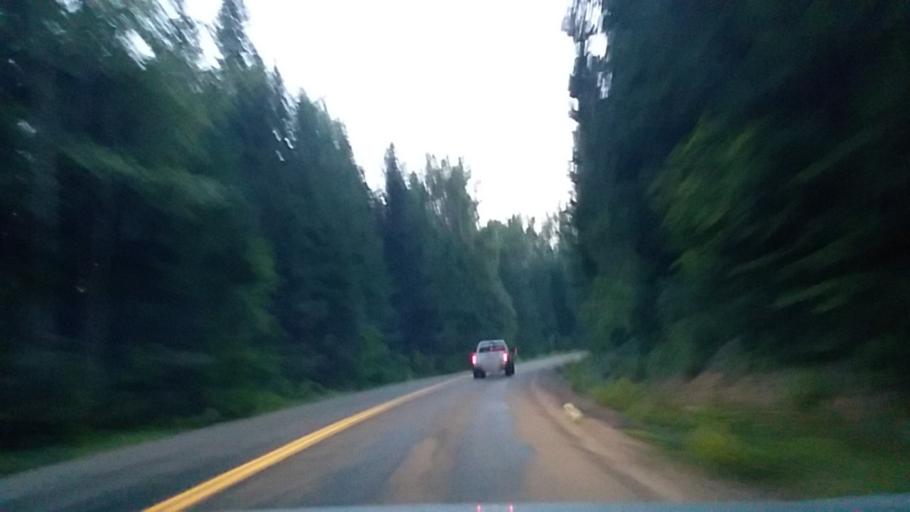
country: US
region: Washington
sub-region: Kittitas County
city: Cle Elum
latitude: 47.3148
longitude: -121.2851
